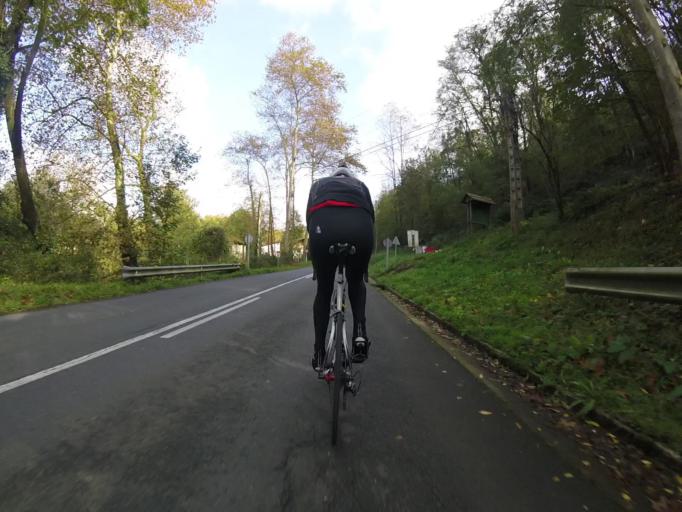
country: ES
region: Basque Country
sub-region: Provincia de Guipuzcoa
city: Hernani
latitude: 43.2505
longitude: -1.9498
